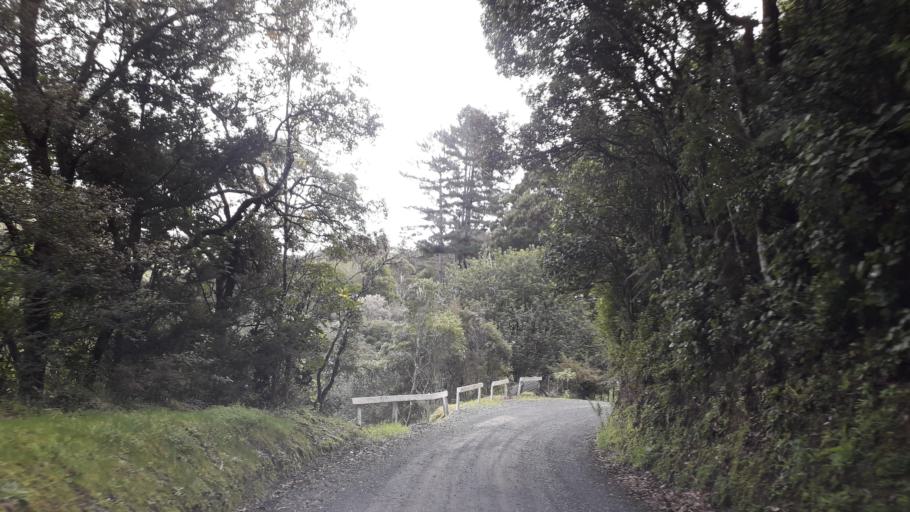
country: NZ
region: Northland
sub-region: Far North District
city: Taipa
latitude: -35.0940
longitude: 173.5366
